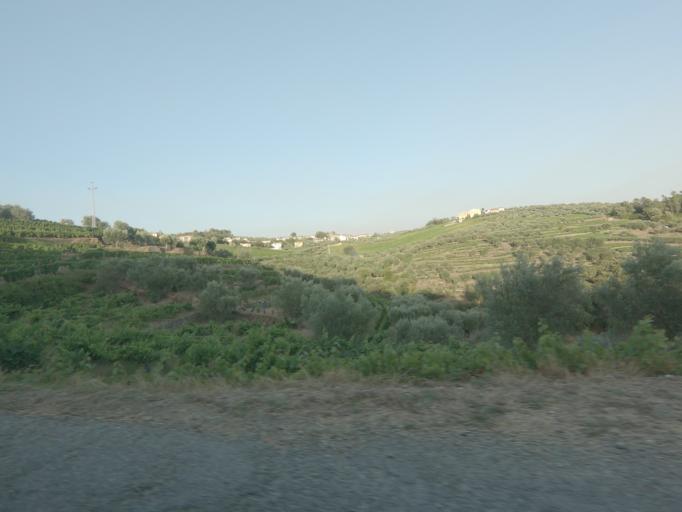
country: PT
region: Viseu
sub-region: Armamar
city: Armamar
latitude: 41.1823
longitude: -7.6896
